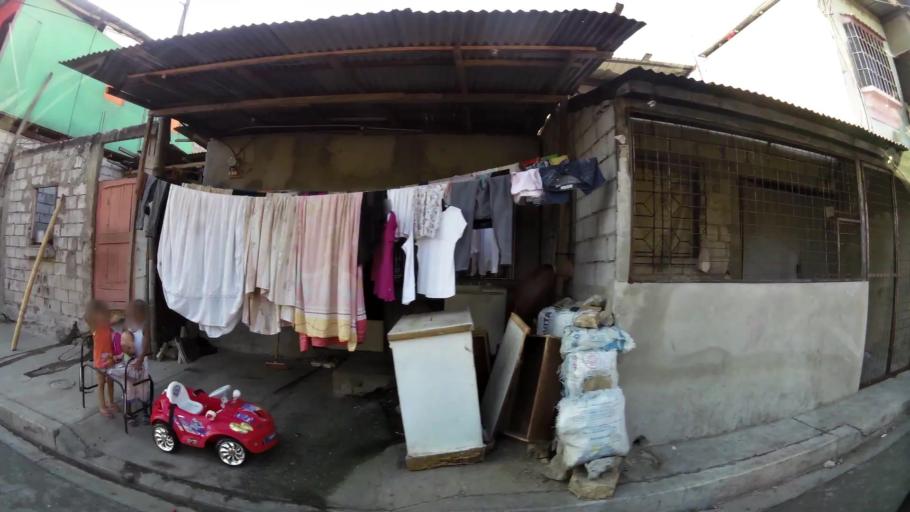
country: EC
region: Guayas
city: Guayaquil
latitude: -2.2234
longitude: -79.9193
